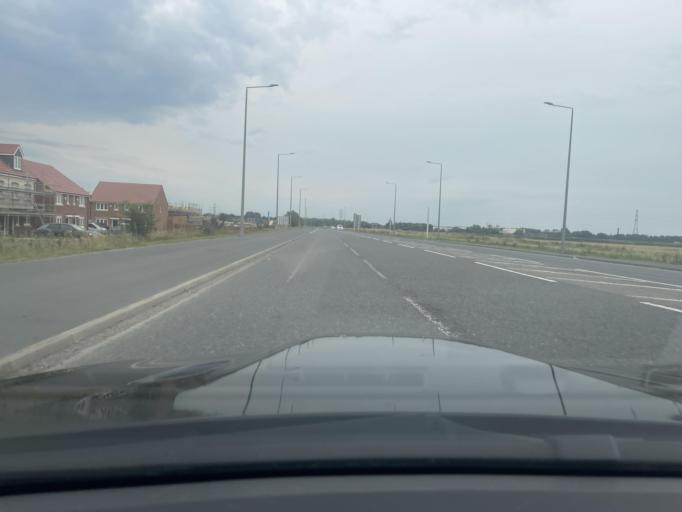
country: GB
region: England
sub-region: Lancashire
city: Leyland
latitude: 53.7126
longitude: -2.7157
